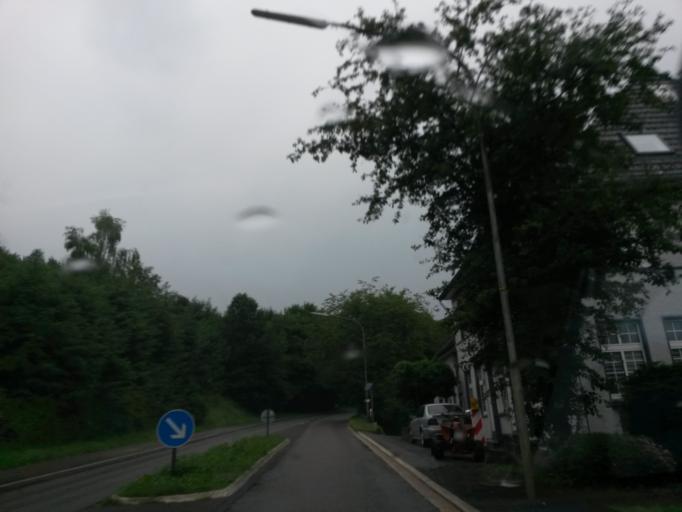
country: DE
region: North Rhine-Westphalia
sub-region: Regierungsbezirk Koln
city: Gummersbach
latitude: 51.0485
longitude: 7.5458
